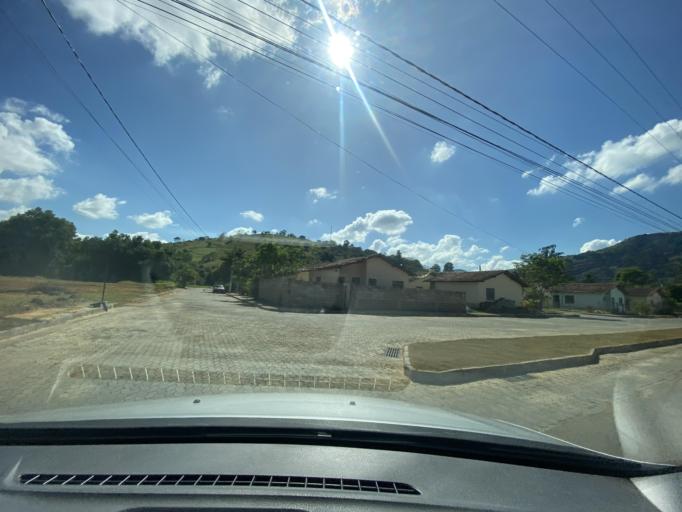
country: BR
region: Espirito Santo
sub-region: Jeronimo Monteiro
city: Jeronimo Monteiro
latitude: -20.7926
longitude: -41.4086
